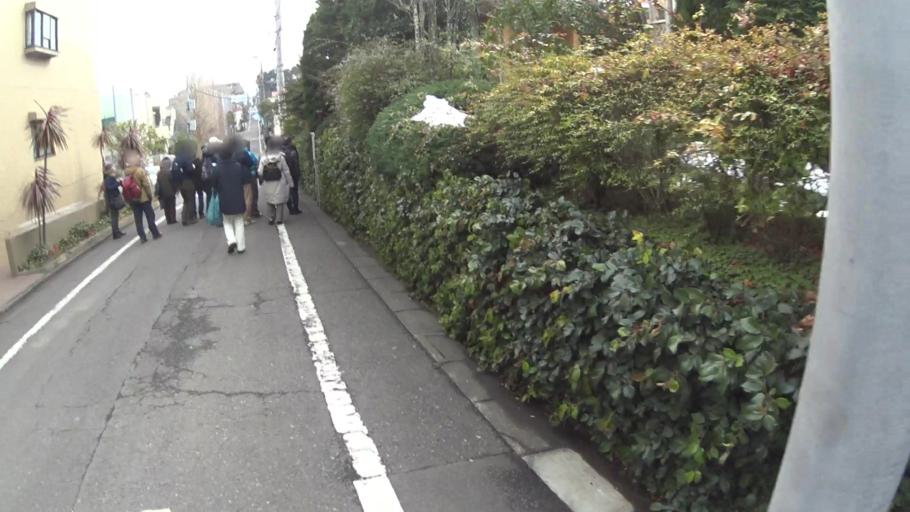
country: JP
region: Tokyo
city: Musashino
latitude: 35.7185
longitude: 139.6020
